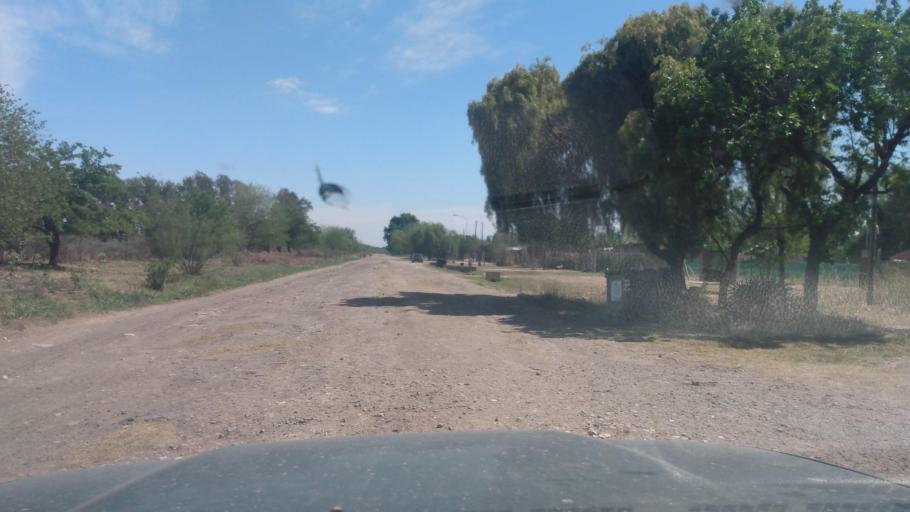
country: AR
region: Buenos Aires
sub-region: Partido de Lujan
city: Lujan
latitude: -34.5481
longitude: -59.1431
